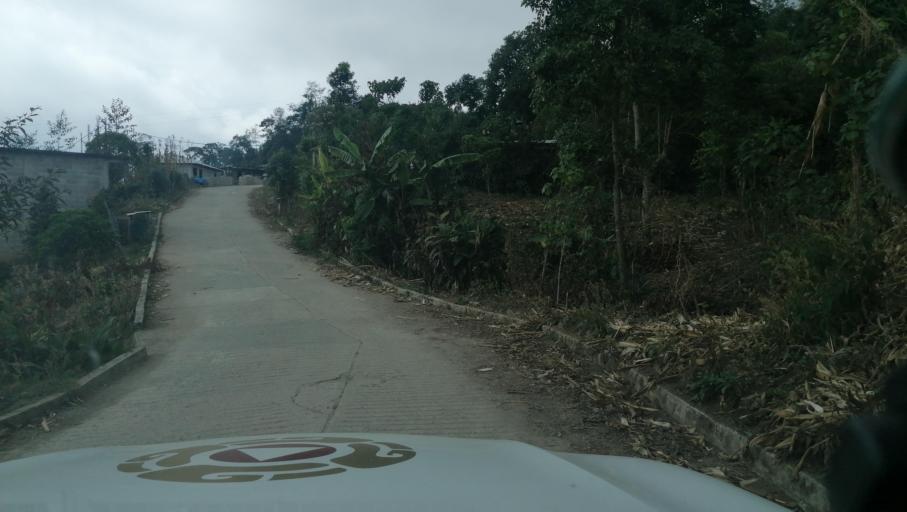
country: GT
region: San Marcos
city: Tacana
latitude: 15.1998
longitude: -92.1780
